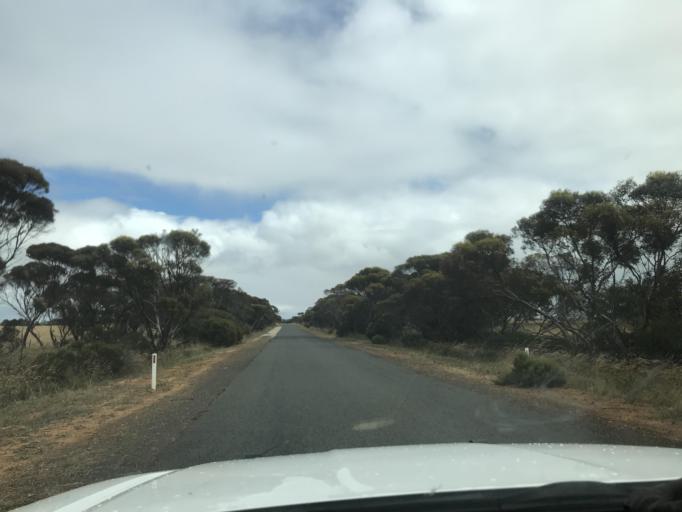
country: AU
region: South Australia
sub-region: Tatiara
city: Bordertown
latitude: -36.1439
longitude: 141.2297
